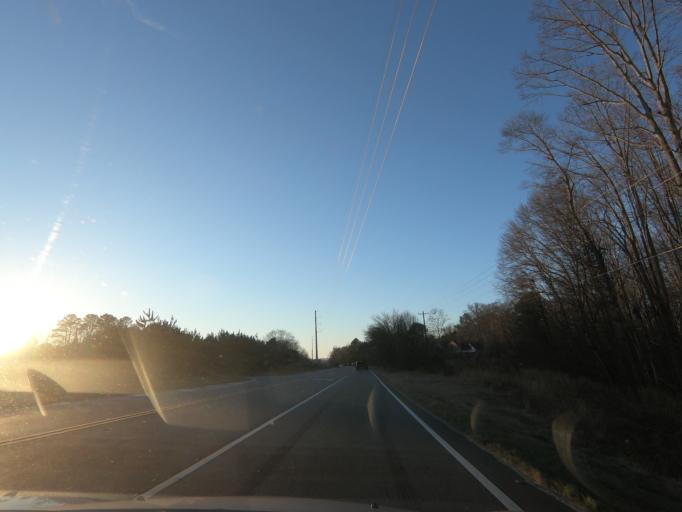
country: US
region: Georgia
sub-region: Forsyth County
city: Cumming
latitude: 34.2990
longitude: -84.1777
